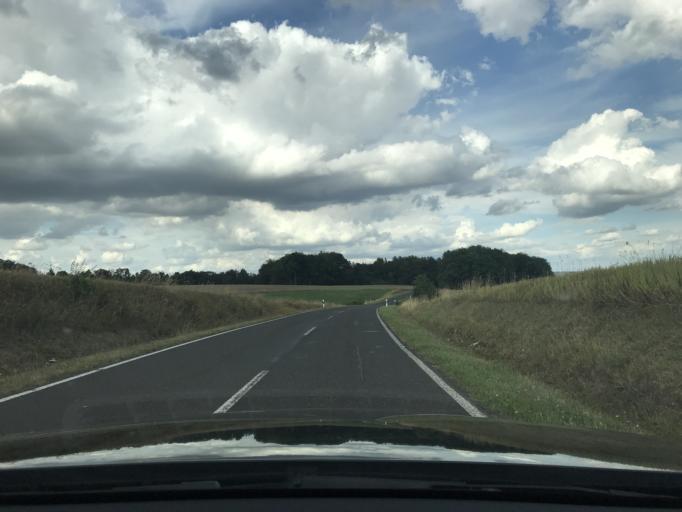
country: DE
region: Bavaria
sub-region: Regierungsbezirk Unterfranken
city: Kirchlauter
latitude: 50.0706
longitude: 10.6776
